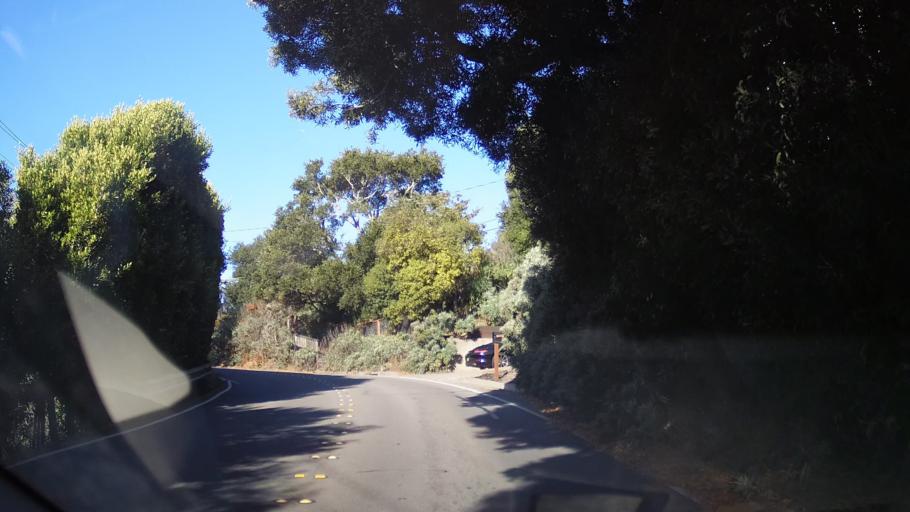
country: US
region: California
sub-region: Marin County
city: Mill Valley
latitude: 37.9002
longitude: -122.5463
